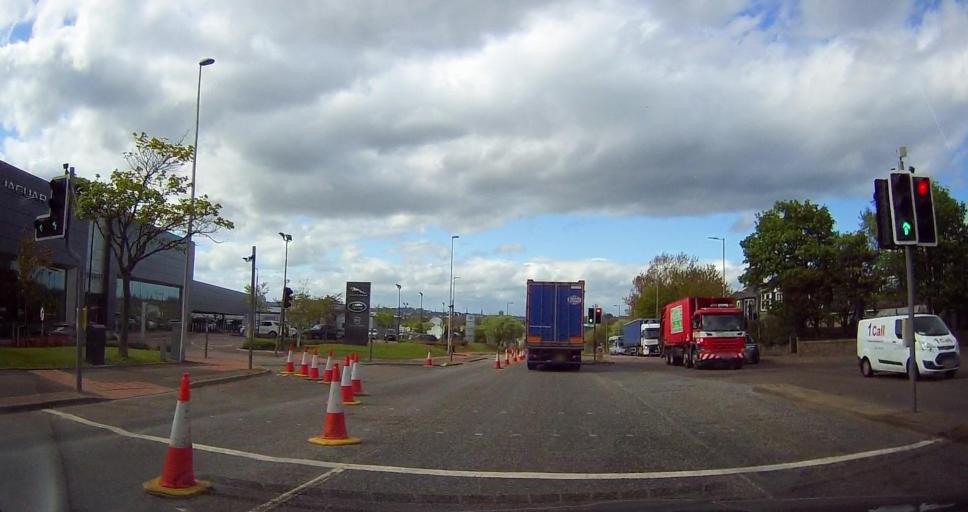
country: GB
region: Scotland
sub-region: Aberdeen City
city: Aberdeen
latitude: 57.1242
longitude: -2.0895
